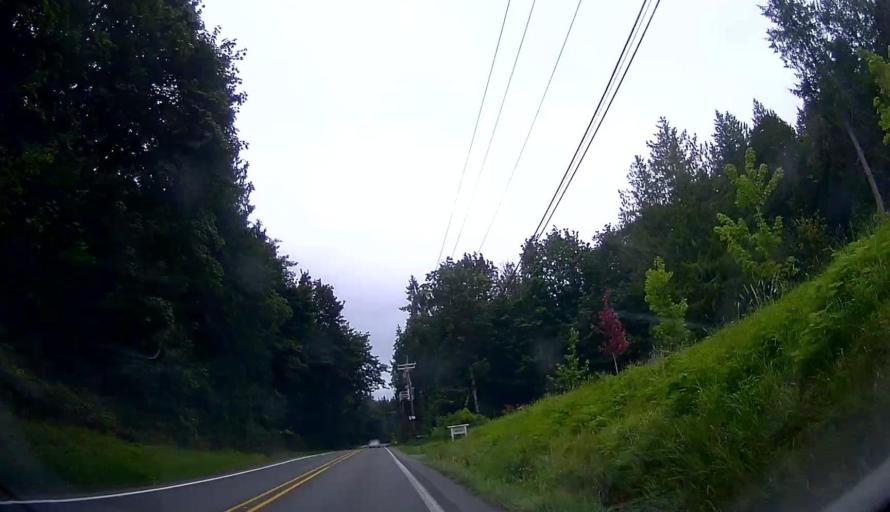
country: US
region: Washington
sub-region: Snohomish County
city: Tulalip
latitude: 48.0979
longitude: -122.3214
